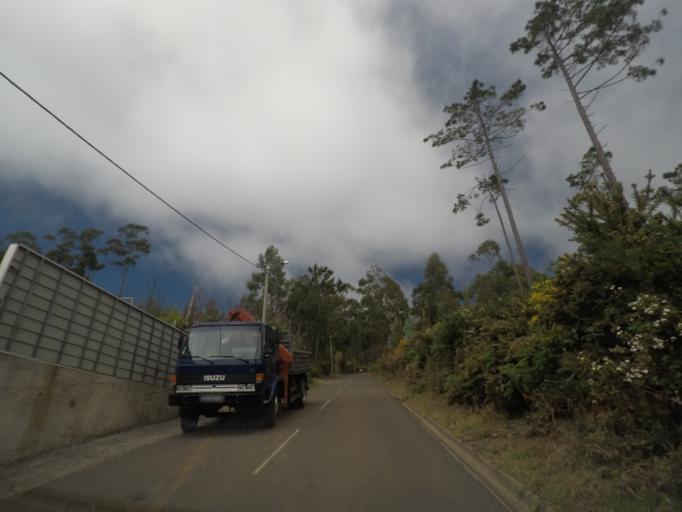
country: PT
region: Madeira
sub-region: Calheta
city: Arco da Calheta
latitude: 32.7191
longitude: -17.1241
